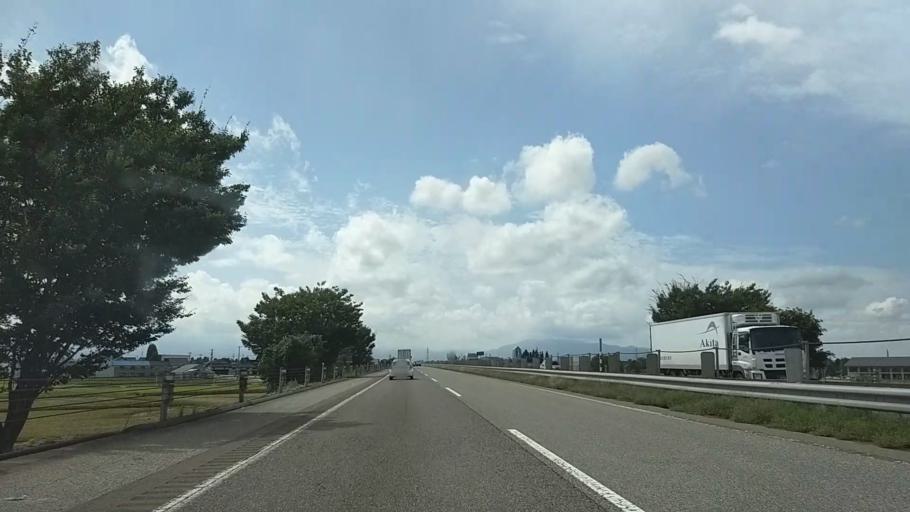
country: JP
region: Toyama
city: Nanto-shi
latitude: 36.6416
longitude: 136.9755
